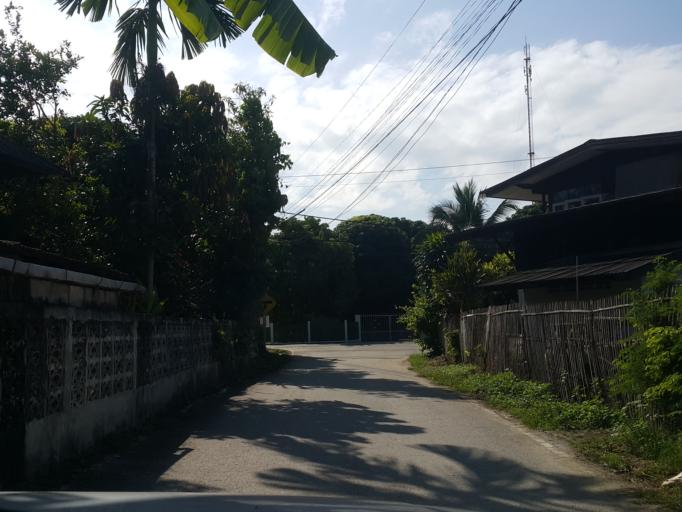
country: TH
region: Chiang Mai
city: Saraphi
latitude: 18.7407
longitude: 99.0531
